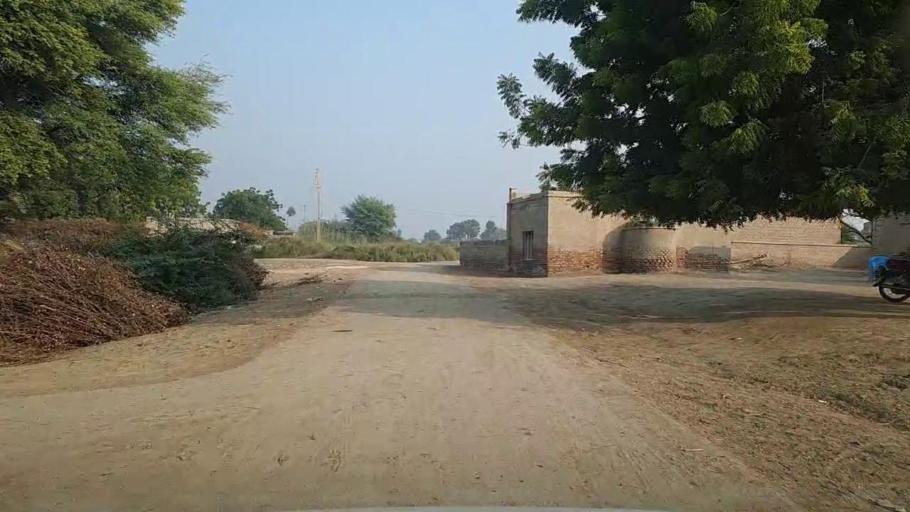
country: PK
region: Sindh
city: Kandiari
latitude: 27.0089
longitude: 68.4910
